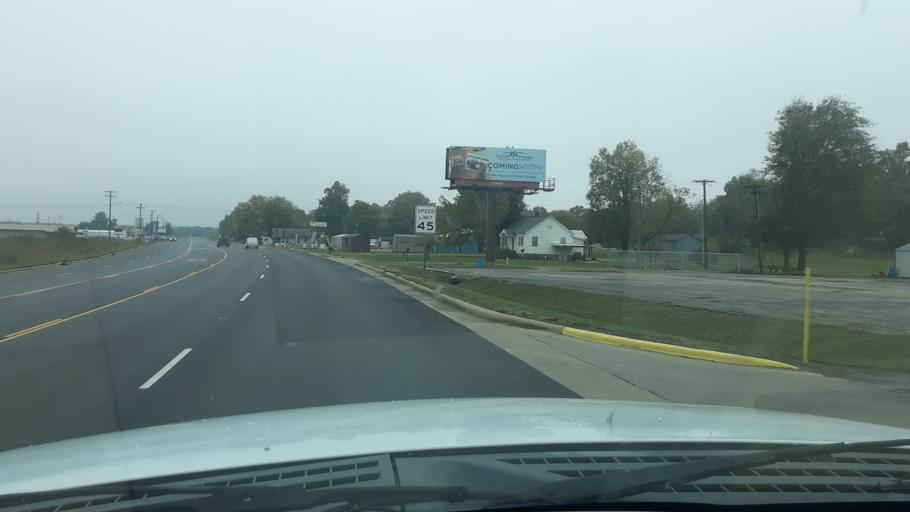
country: US
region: Illinois
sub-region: Saline County
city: Harrisburg
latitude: 37.7675
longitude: -88.5124
